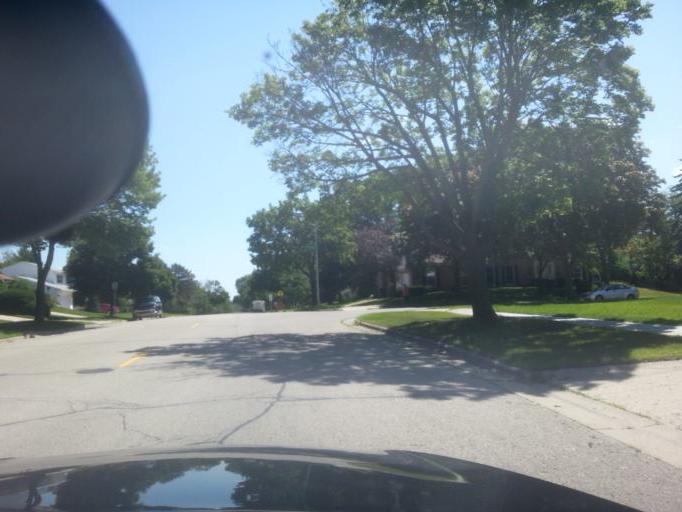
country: US
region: Wisconsin
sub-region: Dane County
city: Middleton
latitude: 43.0676
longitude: -89.4976
